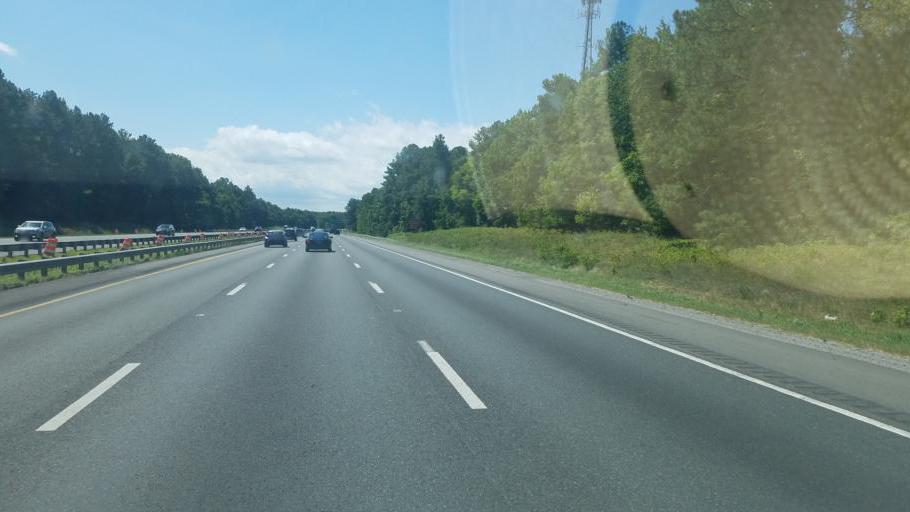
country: US
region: Virginia
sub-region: Spotsylvania County
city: Spotsylvania Courthouse
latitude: 38.1554
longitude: -77.5072
